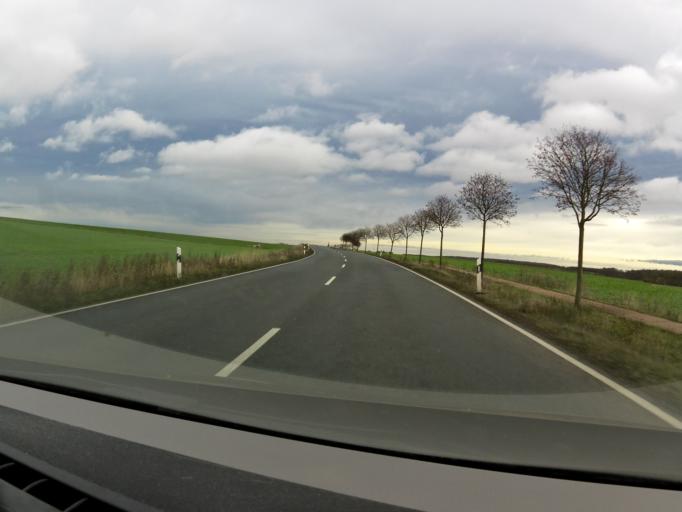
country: DE
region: Saxony-Anhalt
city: Blankenheim
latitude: 51.5407
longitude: 11.3902
